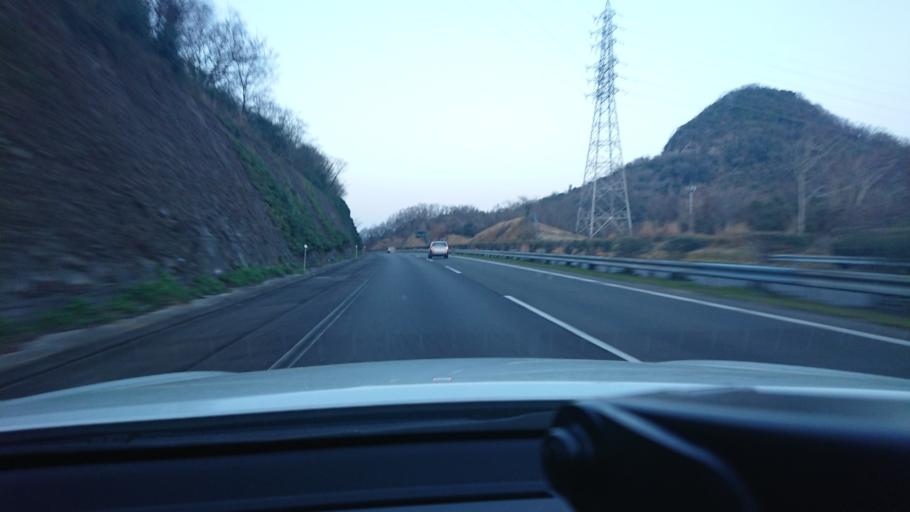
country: JP
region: Kagawa
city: Takamatsu-shi
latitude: 34.2955
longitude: 133.9803
